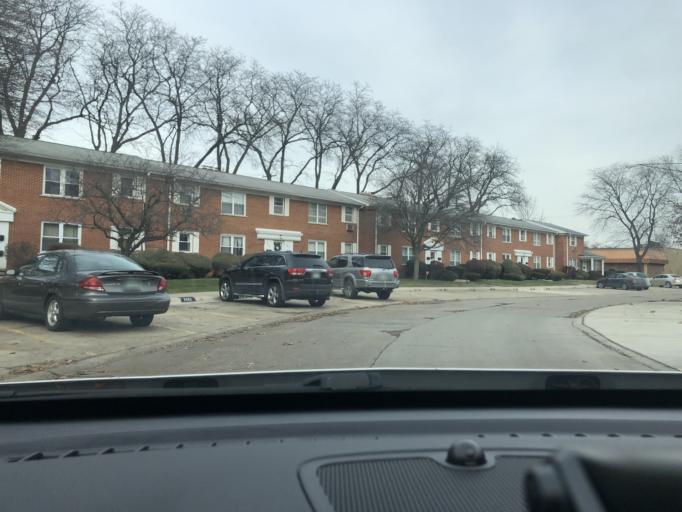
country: US
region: Michigan
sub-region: Wayne County
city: Dearborn Heights
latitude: 42.3411
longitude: -83.2408
